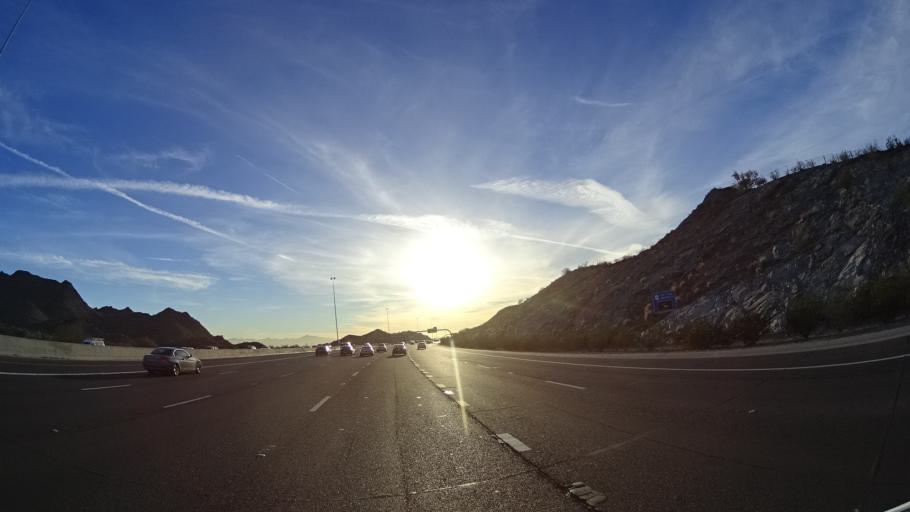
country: US
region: Arizona
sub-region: Maricopa County
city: Paradise Valley
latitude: 33.5683
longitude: -112.0282
